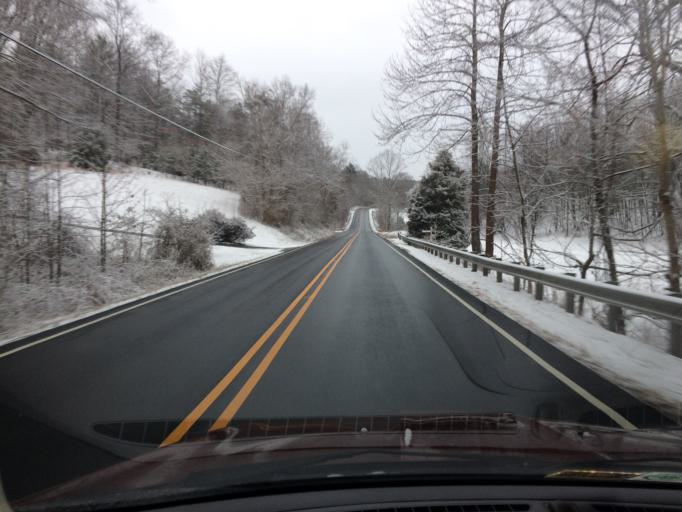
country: US
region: Virginia
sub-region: Amherst County
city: Amherst
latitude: 37.6668
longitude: -79.1738
